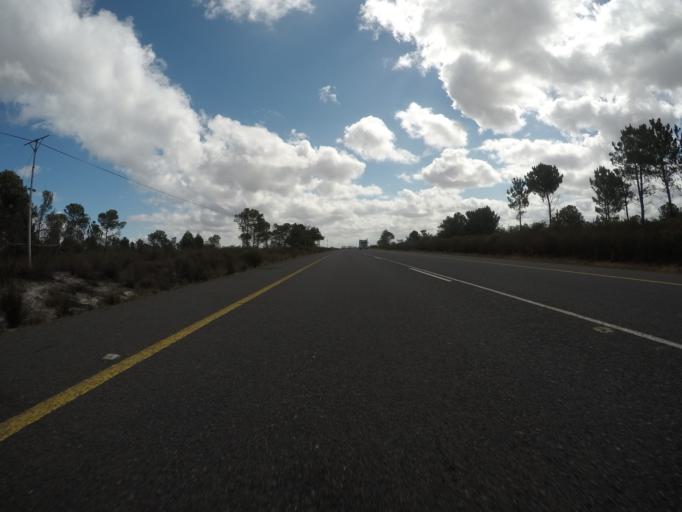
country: ZA
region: Western Cape
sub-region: Eden District Municipality
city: Riversdale
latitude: -34.2126
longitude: 21.5560
